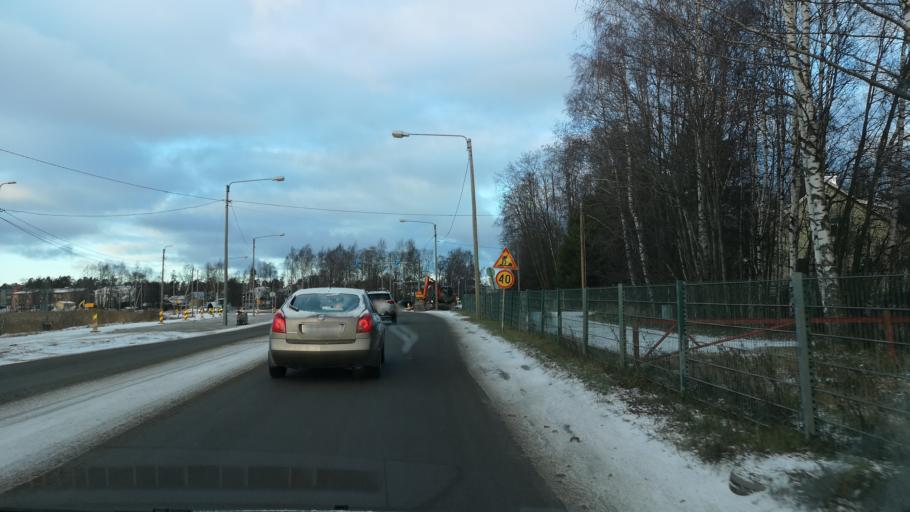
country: FI
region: Ostrobothnia
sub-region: Vaasa
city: Vaasa
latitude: 63.1123
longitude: 21.6187
